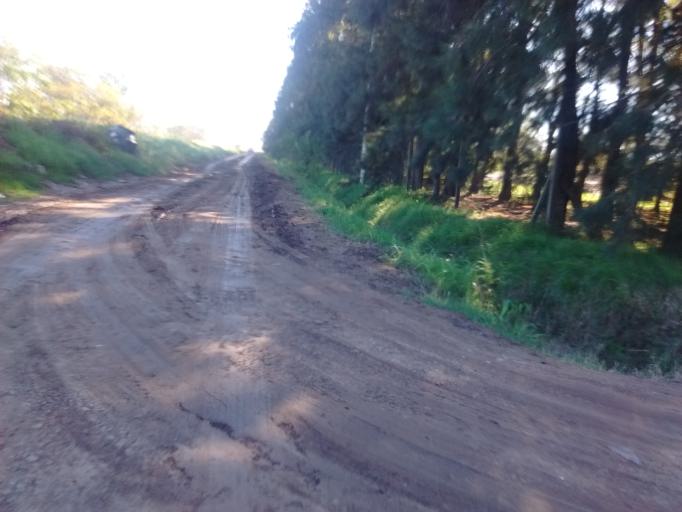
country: AR
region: Santa Fe
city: Roldan
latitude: -32.9503
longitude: -60.8943
